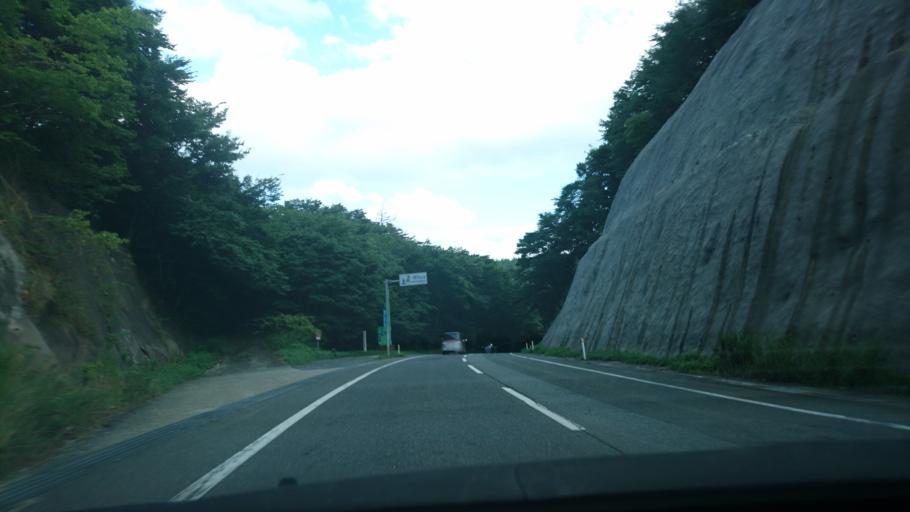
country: JP
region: Iwate
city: Mizusawa
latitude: 39.0597
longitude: 141.2266
